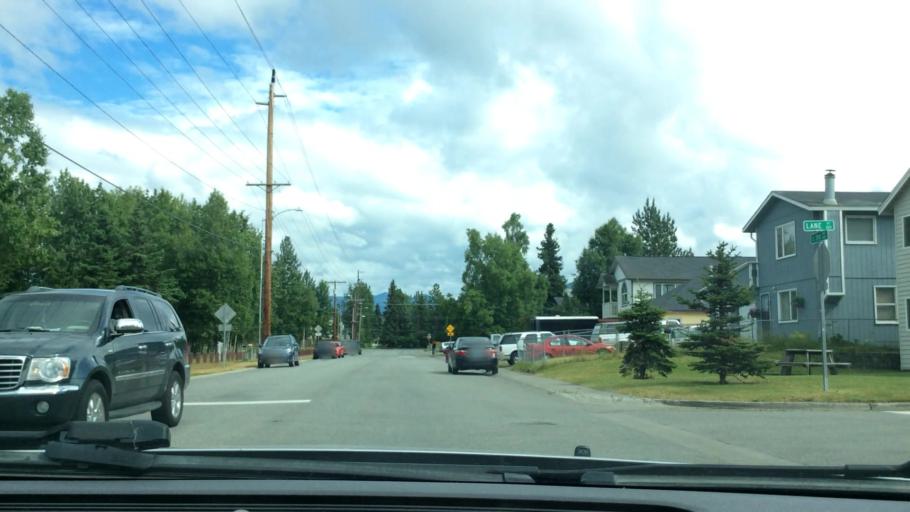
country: US
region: Alaska
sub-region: Anchorage Municipality
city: Anchorage
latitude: 61.2207
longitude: -149.7977
